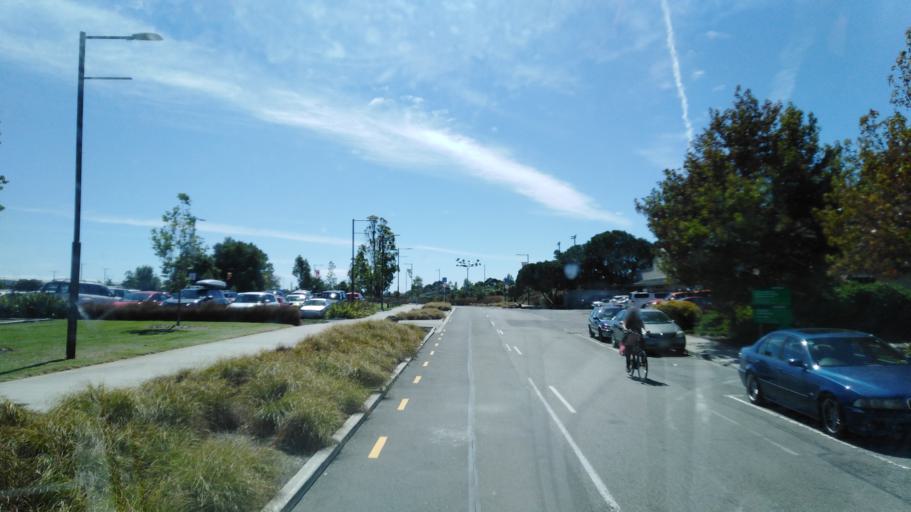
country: NZ
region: Nelson
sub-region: Nelson City
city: Nelson
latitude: -41.2697
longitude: 173.2814
